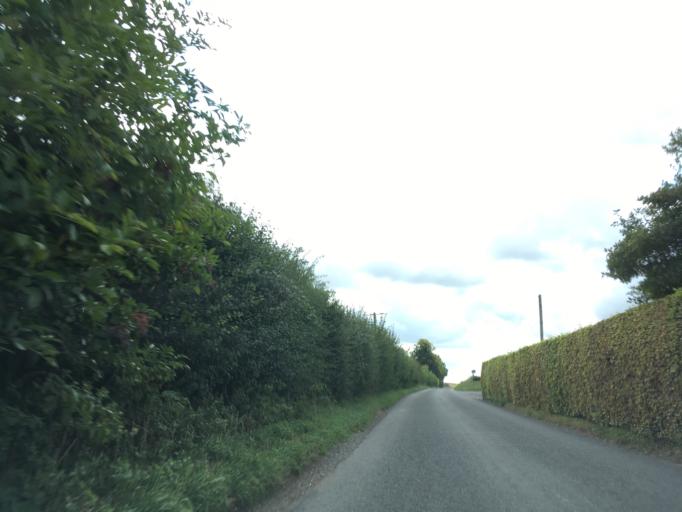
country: GB
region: England
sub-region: Hampshire
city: Overton
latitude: 51.2110
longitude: -1.3738
